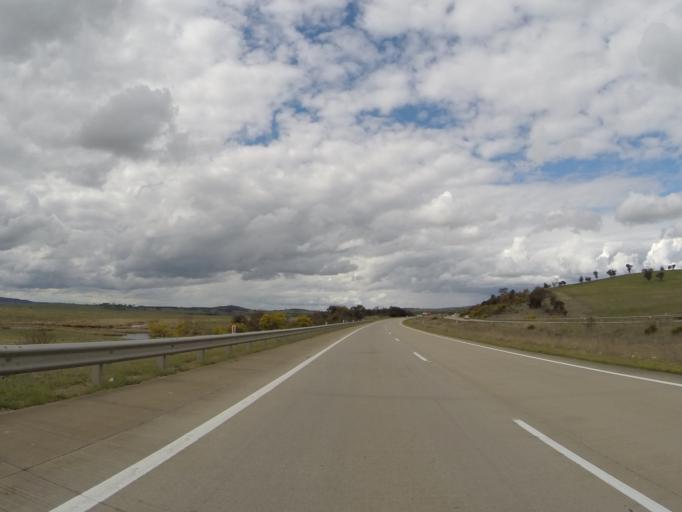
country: AU
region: New South Wales
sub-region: Yass Valley
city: Gundaroo
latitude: -34.8156
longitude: 149.4141
